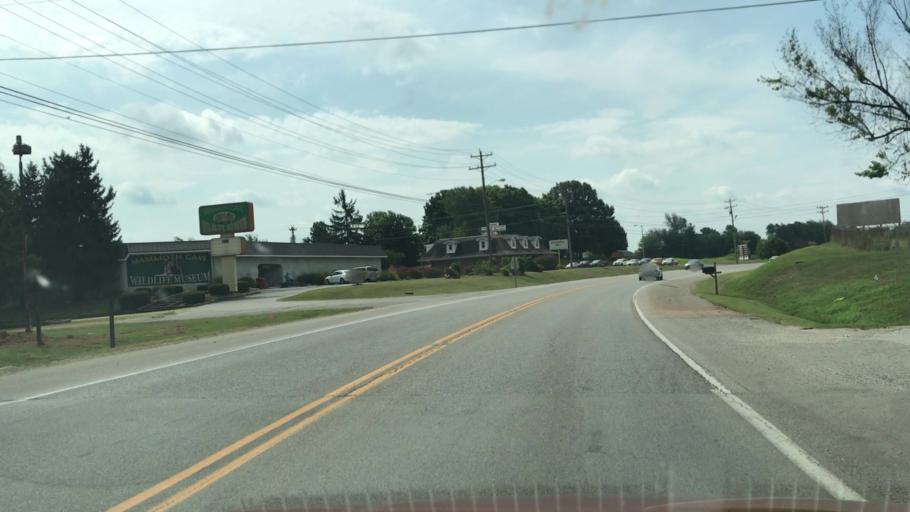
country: US
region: Kentucky
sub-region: Barren County
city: Cave City
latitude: 37.1274
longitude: -85.9623
